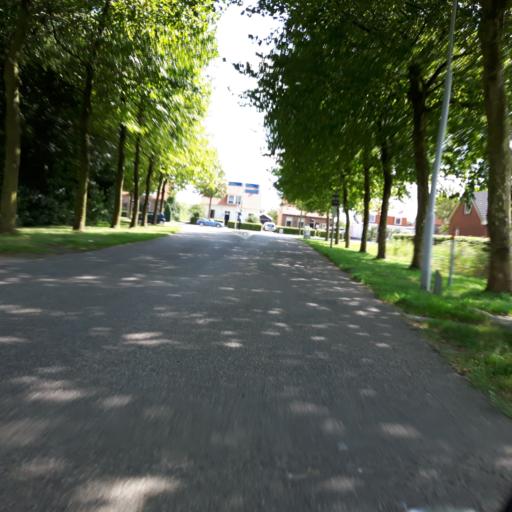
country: NL
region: Zeeland
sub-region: Gemeente Goes
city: Goes
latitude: 51.4569
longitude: 3.8938
